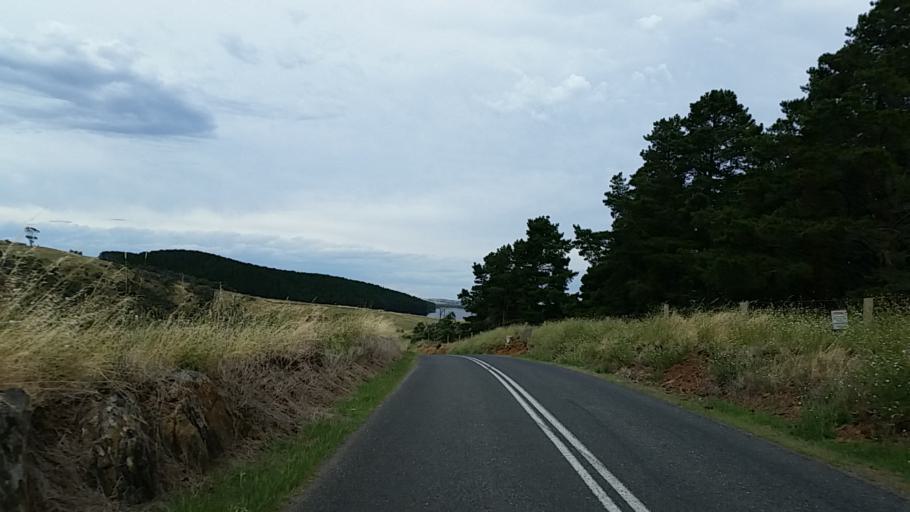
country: AU
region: South Australia
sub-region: Yankalilla
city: Normanville
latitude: -35.4032
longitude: 138.4173
